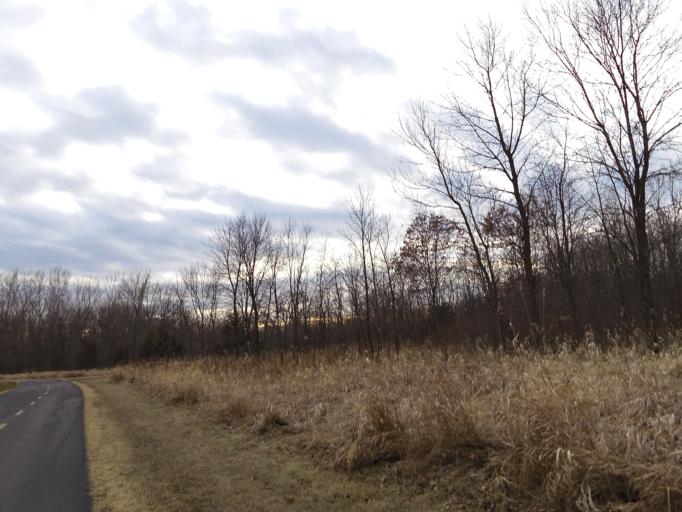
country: US
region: Minnesota
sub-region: Scott County
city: Prior Lake
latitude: 44.6981
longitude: -93.3962
